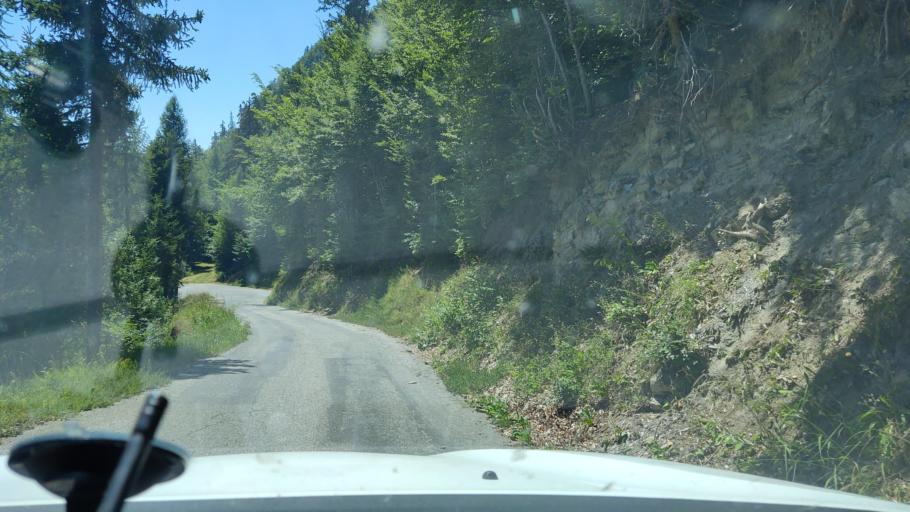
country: FR
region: Rhone-Alpes
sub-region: Departement de la Savoie
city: Salins-les-Thermes
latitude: 45.4644
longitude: 6.5050
